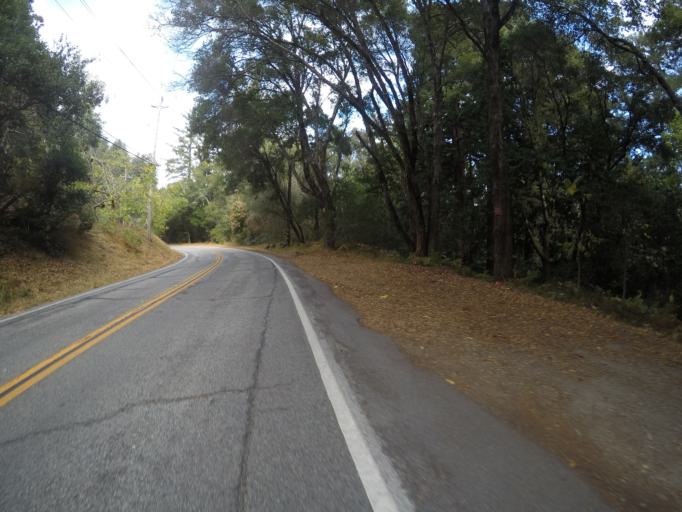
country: US
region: California
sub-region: Santa Cruz County
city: Pasatiempo
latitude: 37.0252
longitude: -122.0254
